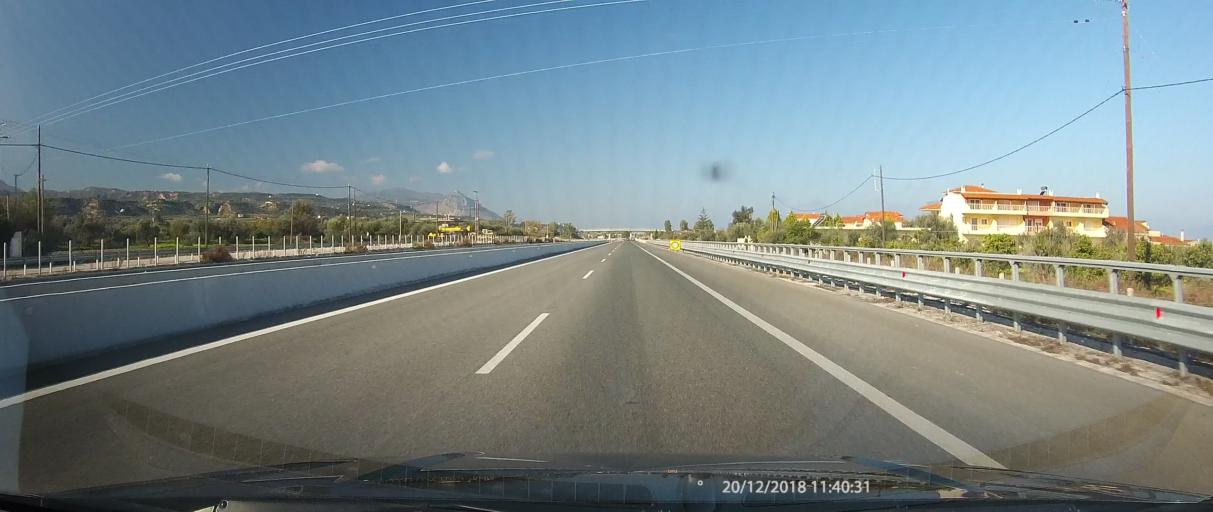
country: GR
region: Peloponnese
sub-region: Nomos Korinthias
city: Xylokastro
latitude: 38.0539
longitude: 22.6760
